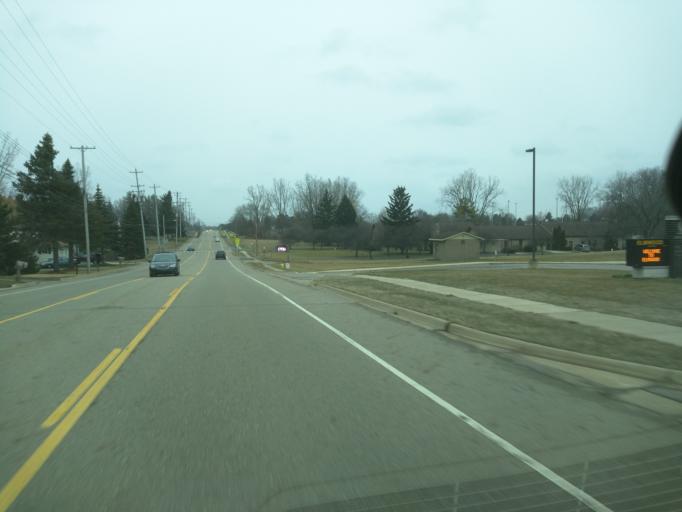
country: US
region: Michigan
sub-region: Eaton County
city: Waverly
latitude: 42.7529
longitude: -84.6225
